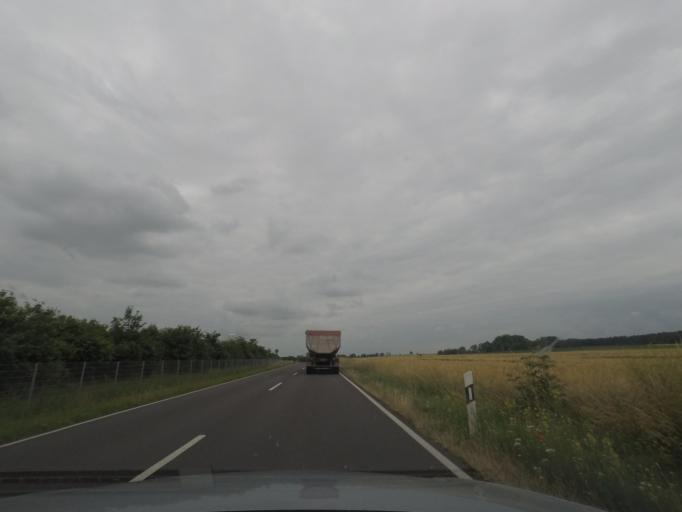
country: DE
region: Saxony-Anhalt
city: Erxleben
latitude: 52.2202
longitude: 11.3036
